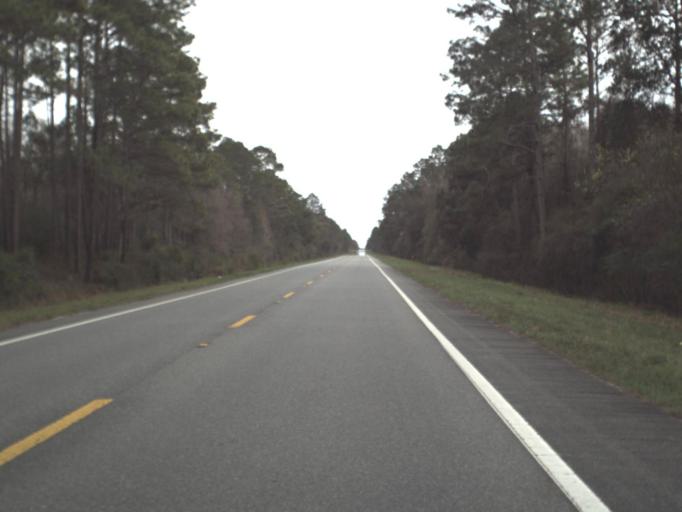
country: US
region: Florida
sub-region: Wakulla County
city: Crawfordville
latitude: 30.3235
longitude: -84.4559
